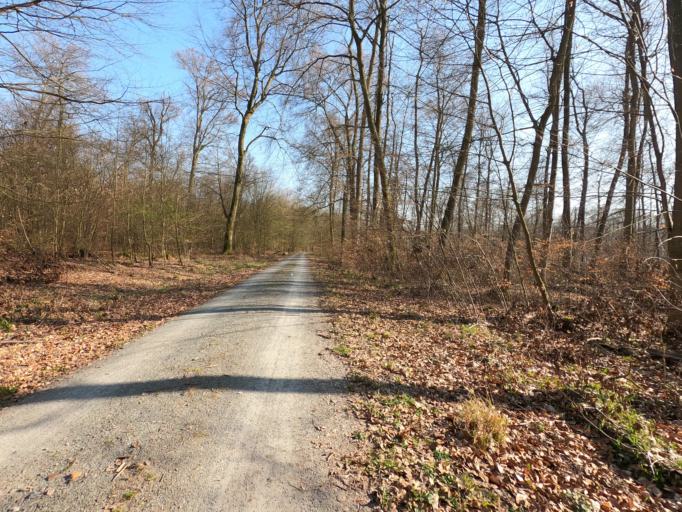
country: DE
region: Hesse
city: Morfelden-Walldorf
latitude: 49.9595
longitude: 8.5553
